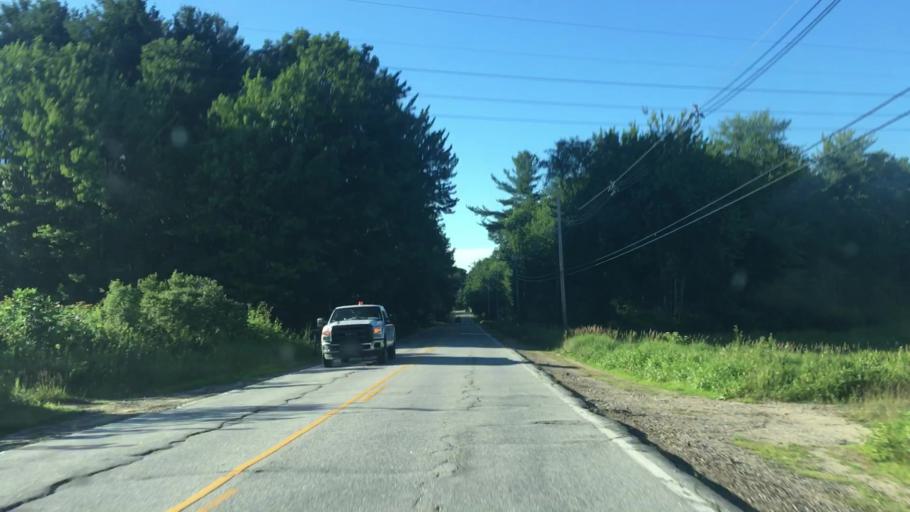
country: US
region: New Hampshire
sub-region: Rockingham County
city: Sandown
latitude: 42.9469
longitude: -71.1955
